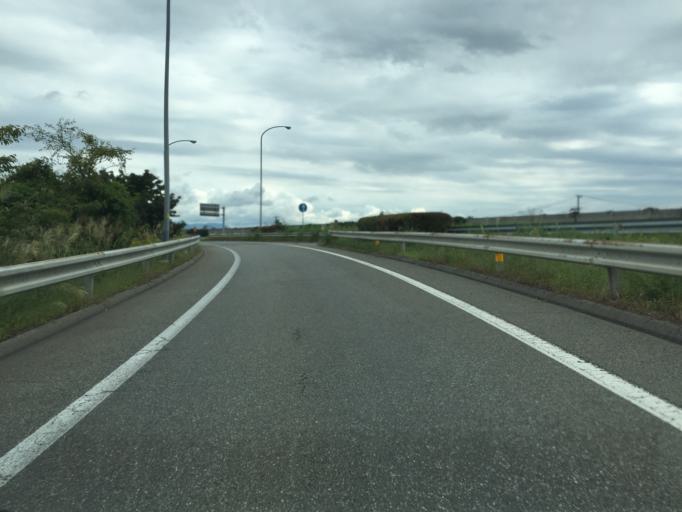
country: JP
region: Fukushima
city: Fukushima-shi
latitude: 37.8034
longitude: 140.4564
